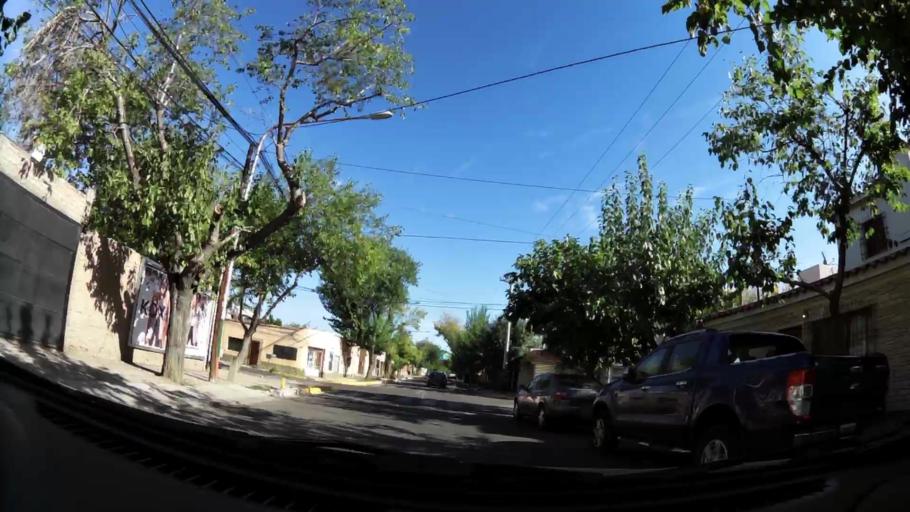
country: AR
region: Mendoza
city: Mendoza
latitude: -32.9017
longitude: -68.8327
